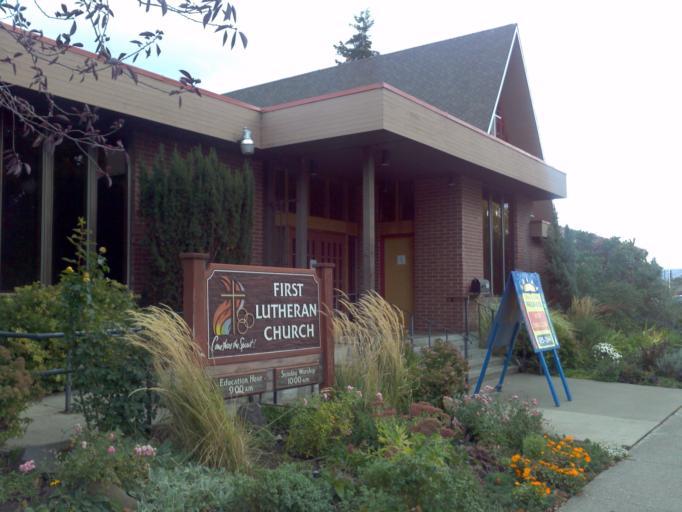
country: US
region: Washington
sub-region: Kittitas County
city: Ellensburg
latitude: 46.9973
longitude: -120.5446
